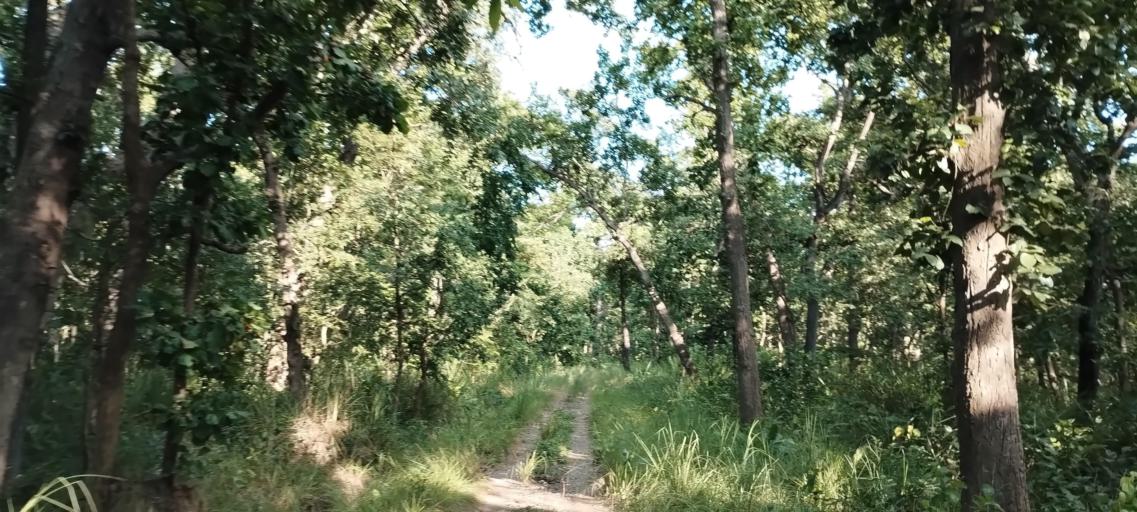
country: NP
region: Far Western
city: Tikapur
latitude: 28.5219
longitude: 81.2715
